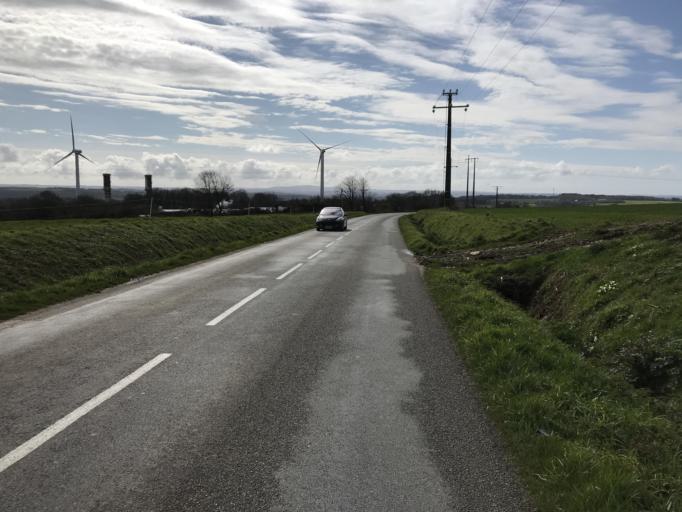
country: FR
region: Brittany
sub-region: Departement du Finistere
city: Dirinon
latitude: 48.3947
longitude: -4.2651
